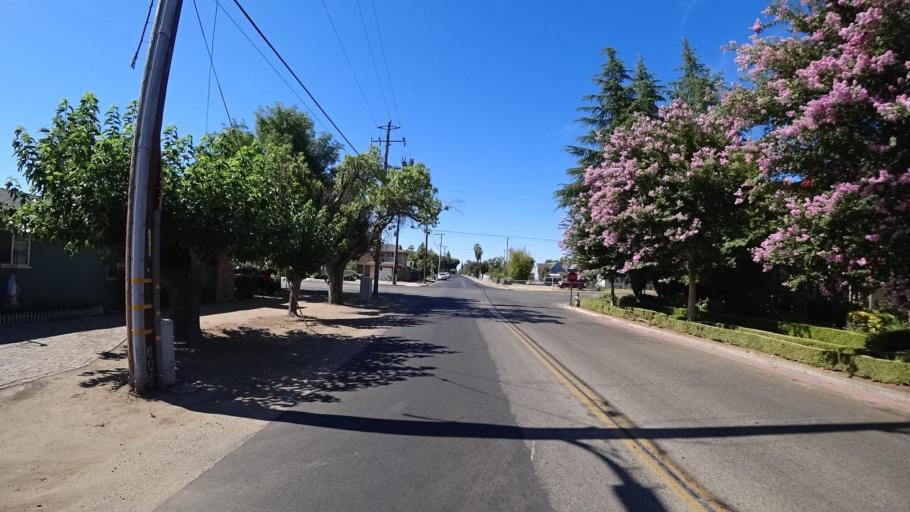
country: US
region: California
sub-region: Fresno County
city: Sunnyside
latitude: 36.7435
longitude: -119.7092
